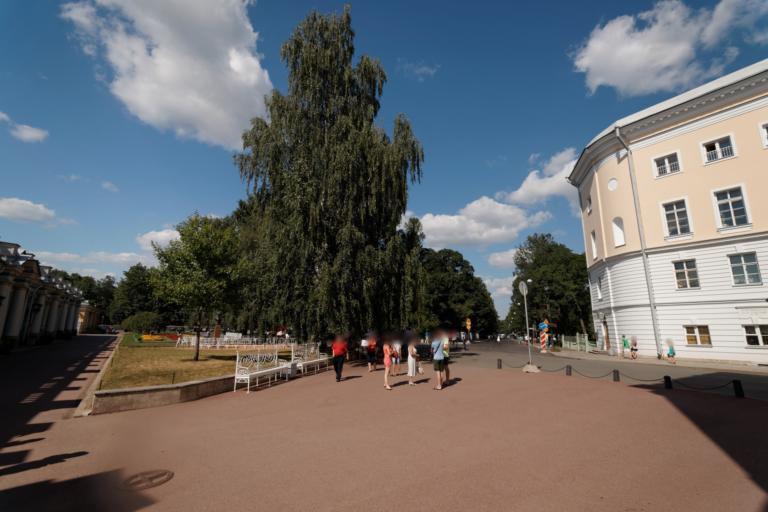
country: RU
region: St.-Petersburg
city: Pushkin
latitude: 59.7173
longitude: 30.3960
